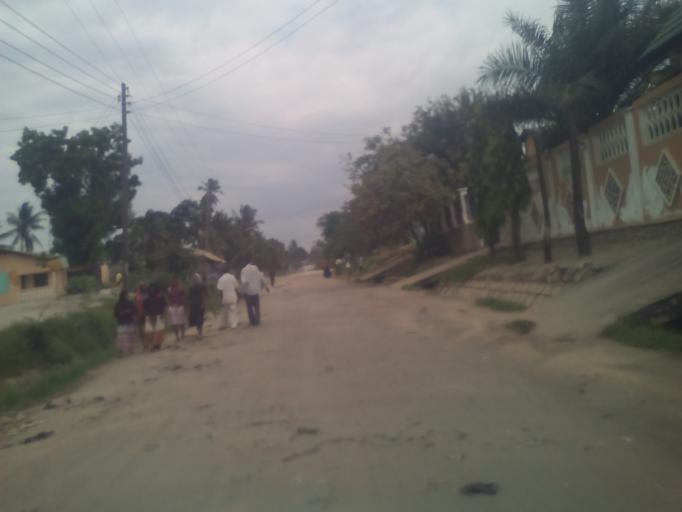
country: TZ
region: Dar es Salaam
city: Dar es Salaam
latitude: -6.8720
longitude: 39.2283
